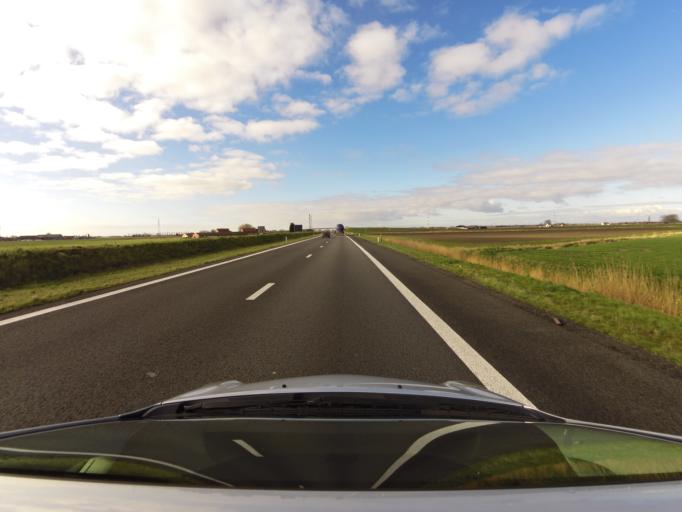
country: BE
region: Flanders
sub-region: Provincie West-Vlaanderen
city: Nieuwpoort
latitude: 51.0992
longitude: 2.7377
